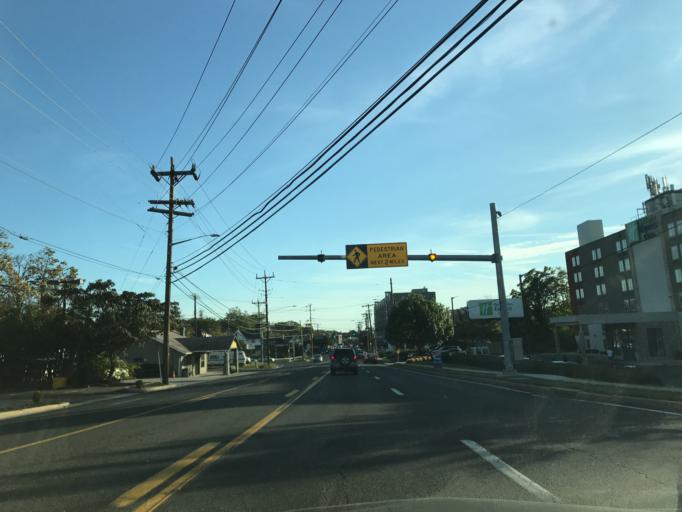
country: US
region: Maryland
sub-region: Prince George's County
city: College Park
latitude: 39.0000
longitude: -76.9314
